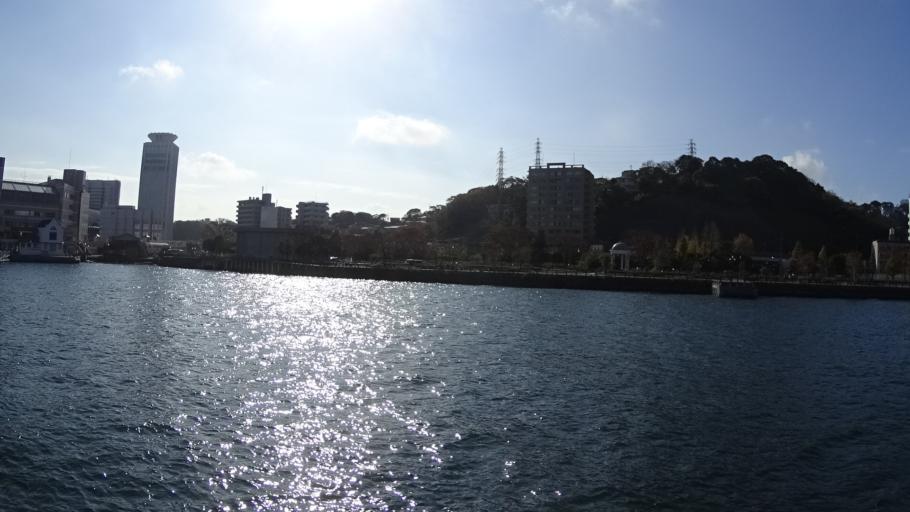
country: JP
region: Kanagawa
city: Yokosuka
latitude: 35.2845
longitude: 139.6597
